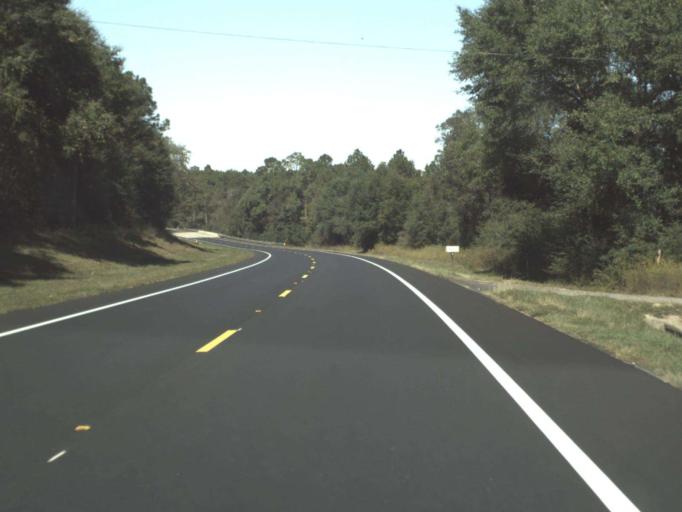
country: US
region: Florida
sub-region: Walton County
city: DeFuniak Springs
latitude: 30.8139
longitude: -86.2035
